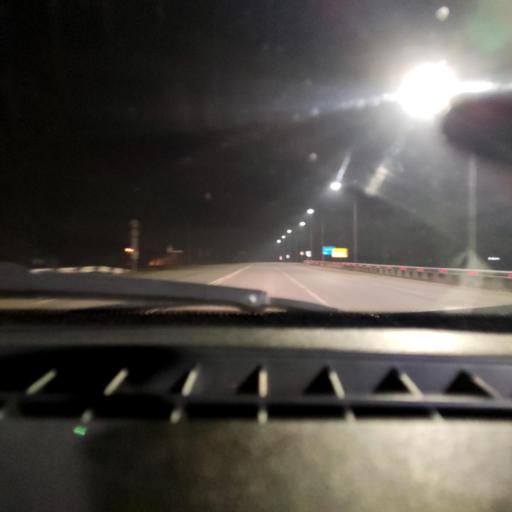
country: RU
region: Bashkortostan
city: Kushnarenkovo
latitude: 55.1006
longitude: 55.3336
